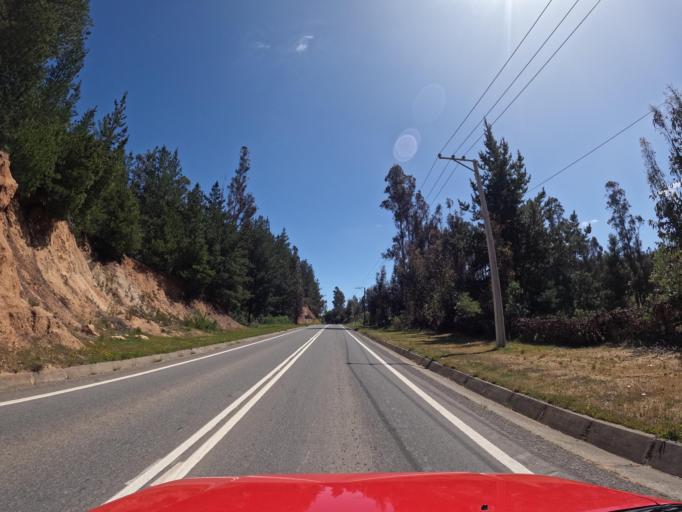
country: CL
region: O'Higgins
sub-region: Provincia de Colchagua
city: Santa Cruz
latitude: -34.6810
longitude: -71.7906
